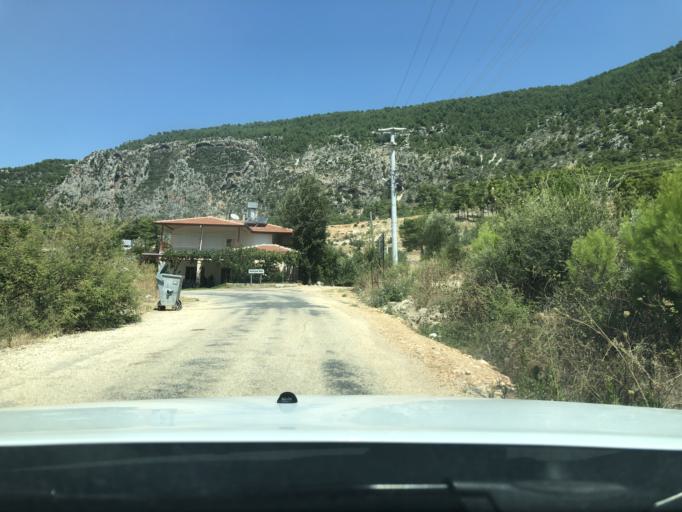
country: TR
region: Antalya
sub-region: Manavgat
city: Manavgat
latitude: 36.8830
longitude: 31.5498
